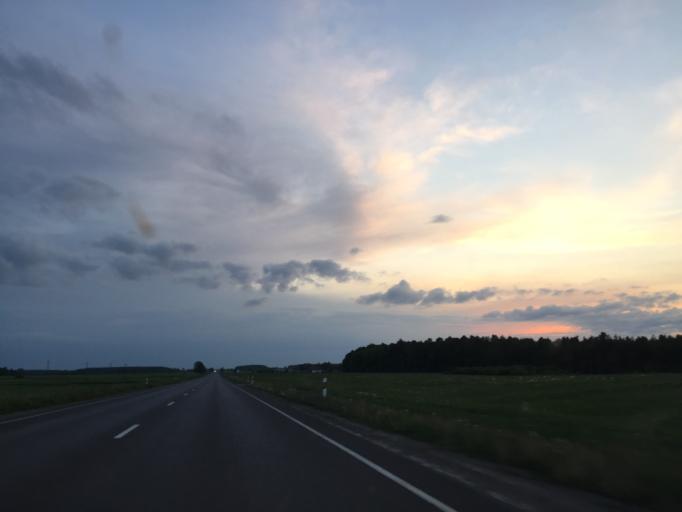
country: LT
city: Vieksniai
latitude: 55.9983
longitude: 22.4912
